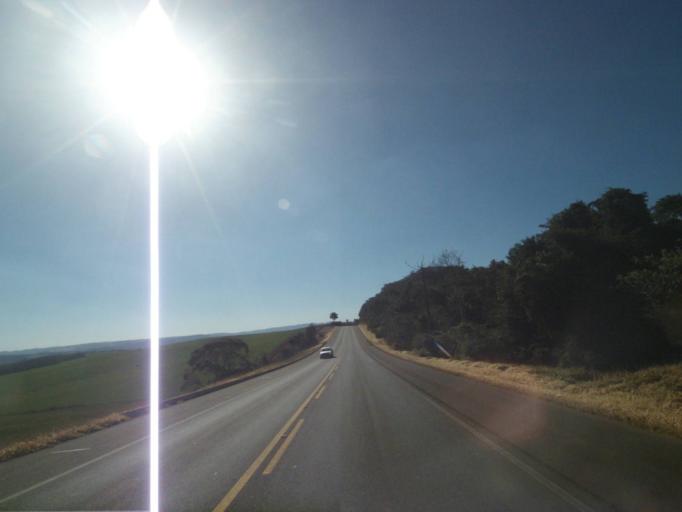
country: BR
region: Parana
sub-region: Tibagi
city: Tibagi
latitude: -24.7132
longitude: -50.4495
